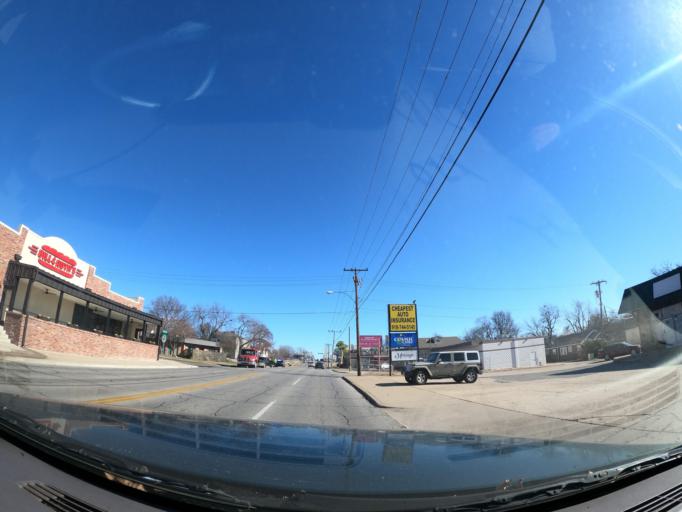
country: US
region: Oklahoma
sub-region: Tulsa County
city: Tulsa
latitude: 36.1405
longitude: -95.9519
